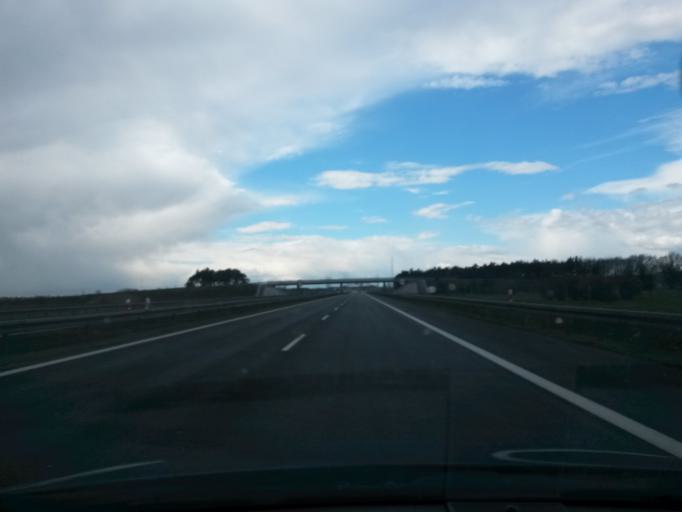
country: PL
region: Greater Poland Voivodeship
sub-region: Powiat slupecki
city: Ladek
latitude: 52.2189
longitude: 17.9620
